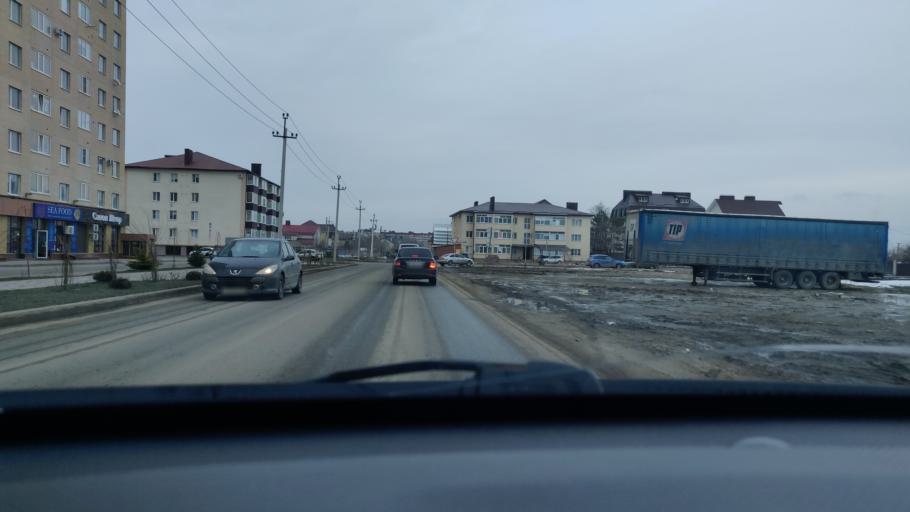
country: RU
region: Stavropol'skiy
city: Tatarka
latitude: 45.0097
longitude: 41.9025
